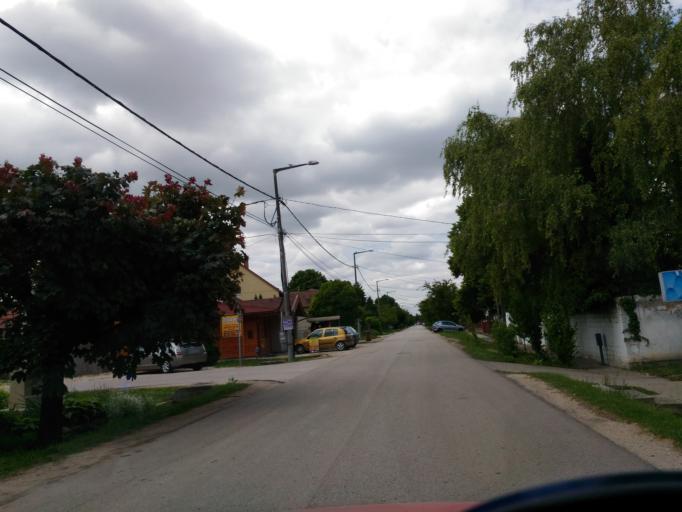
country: HU
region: Fejer
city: Gardony
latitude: 47.2045
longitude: 18.6255
